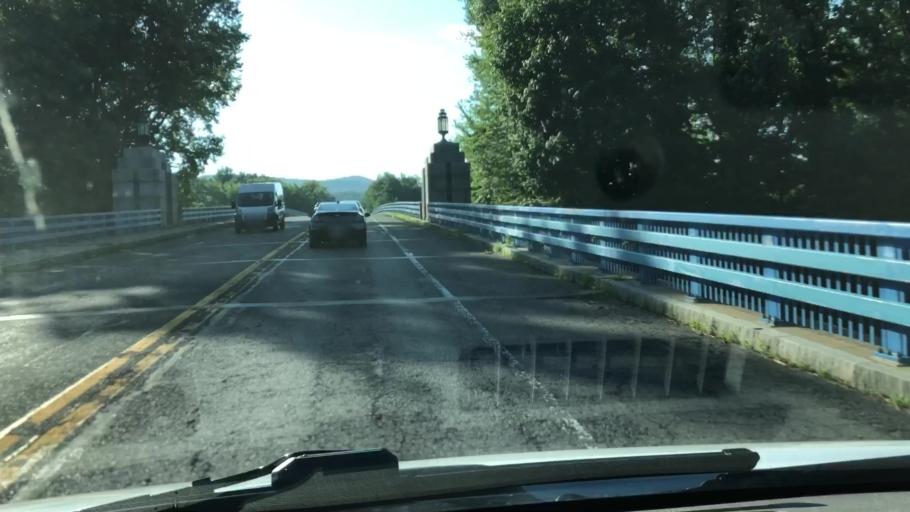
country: US
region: Massachusetts
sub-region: Franklin County
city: South Deerfield
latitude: 42.4683
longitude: -72.5869
